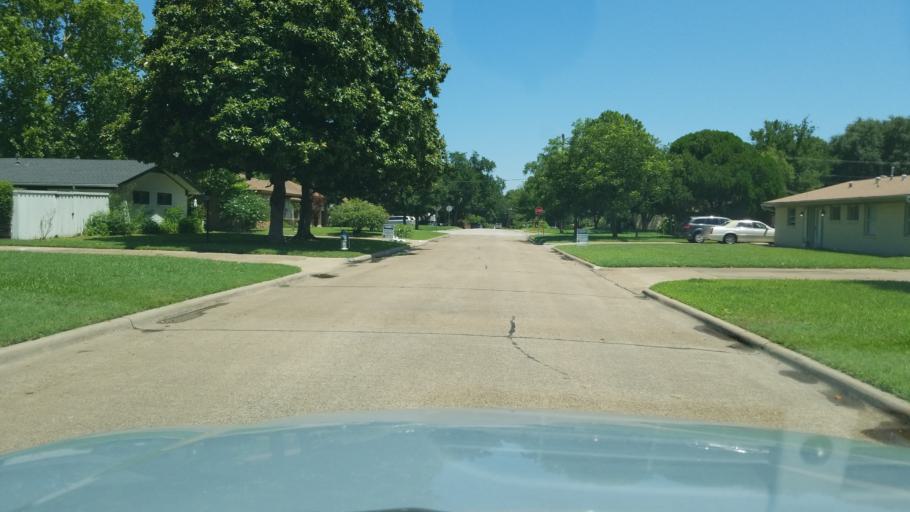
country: US
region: Texas
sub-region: Dallas County
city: Irving
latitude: 32.8057
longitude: -96.9159
